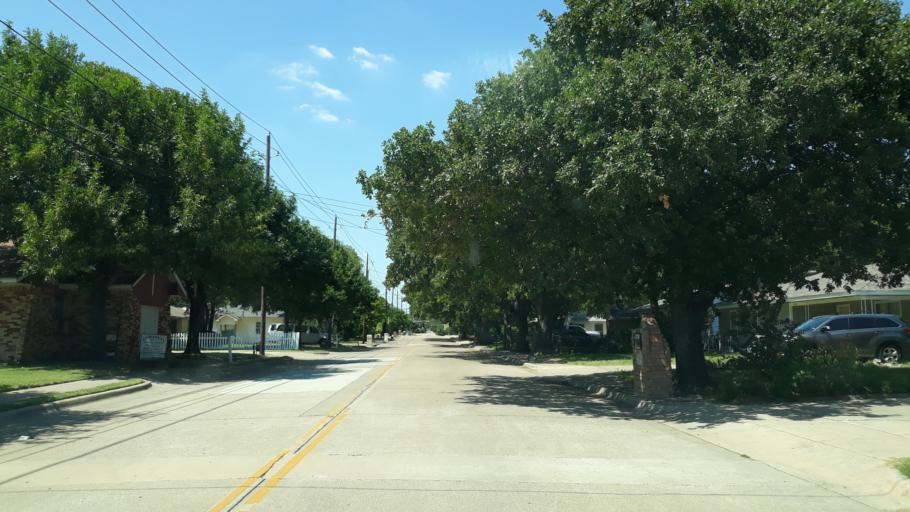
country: US
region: Texas
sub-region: Dallas County
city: Irving
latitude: 32.8193
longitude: -97.0024
